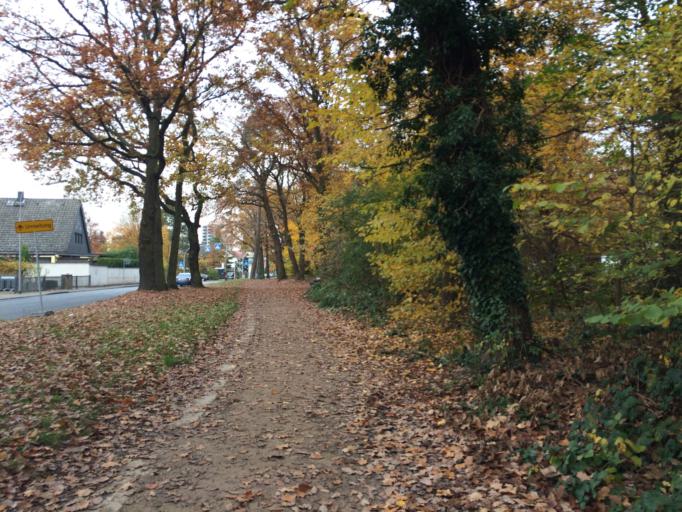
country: DE
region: Hesse
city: Morfelden-Walldorf
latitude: 50.0075
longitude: 8.5820
